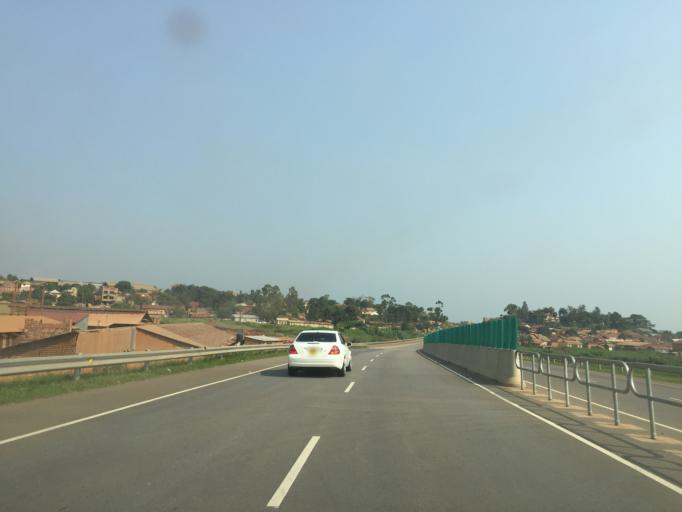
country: UG
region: Central Region
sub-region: Wakiso District
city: Kajansi
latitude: 0.2119
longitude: 32.5428
